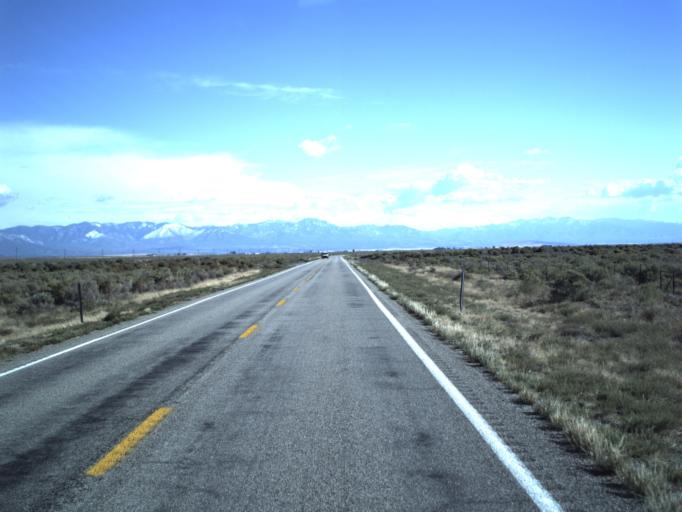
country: US
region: Utah
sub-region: Millard County
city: Delta
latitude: 39.2634
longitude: -112.4490
